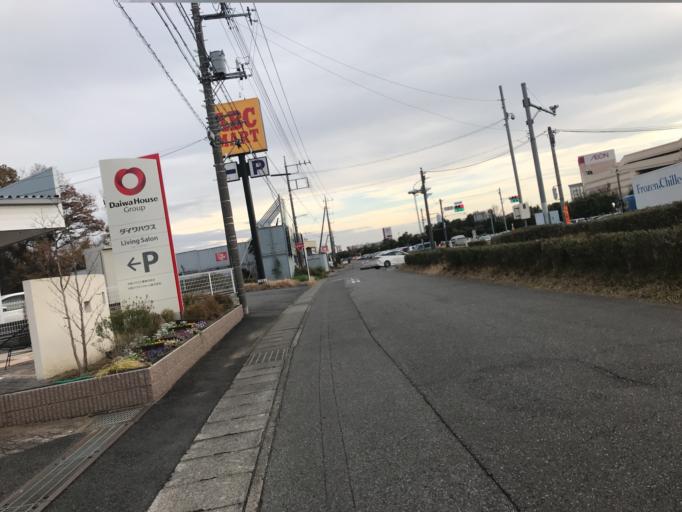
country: JP
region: Gunma
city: Ota
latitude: 36.2974
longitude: 139.4009
